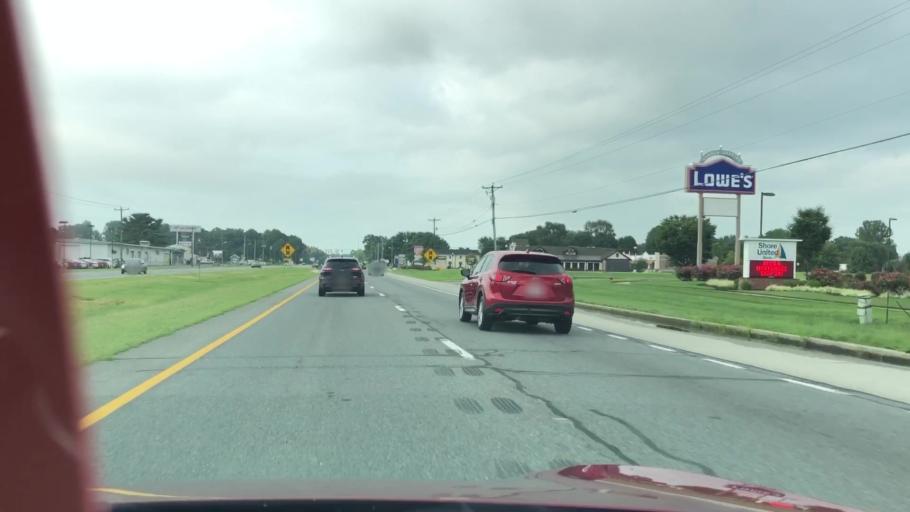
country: US
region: Delaware
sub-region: Kent County
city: Camden
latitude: 39.0977
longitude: -75.5448
